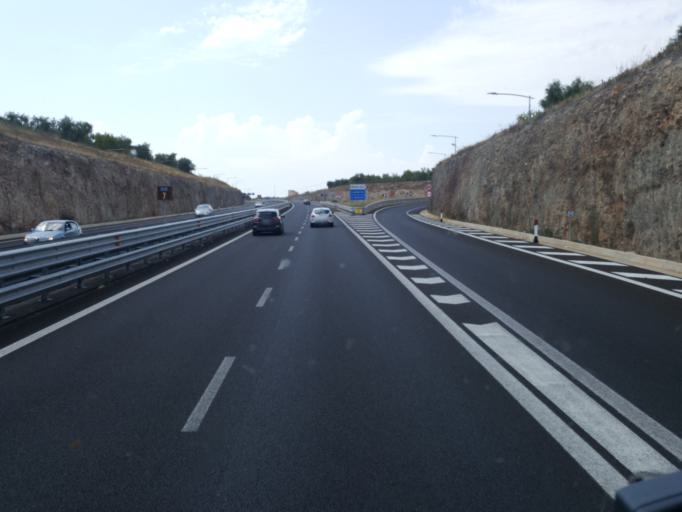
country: IT
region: Apulia
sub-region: Provincia di Bari
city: Palo del Colle
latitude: 41.0464
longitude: 16.7074
